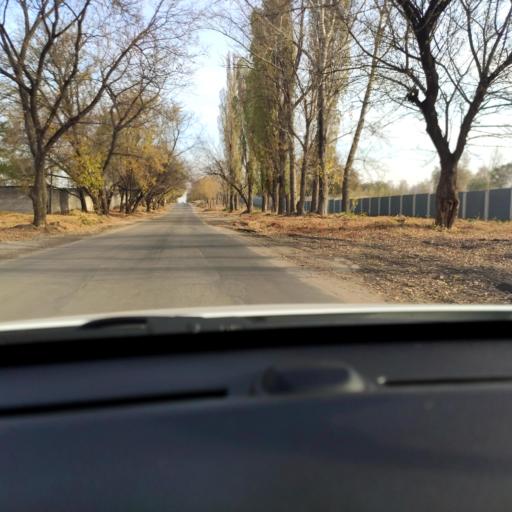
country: RU
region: Voronezj
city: Voronezh
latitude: 51.6591
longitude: 39.2865
